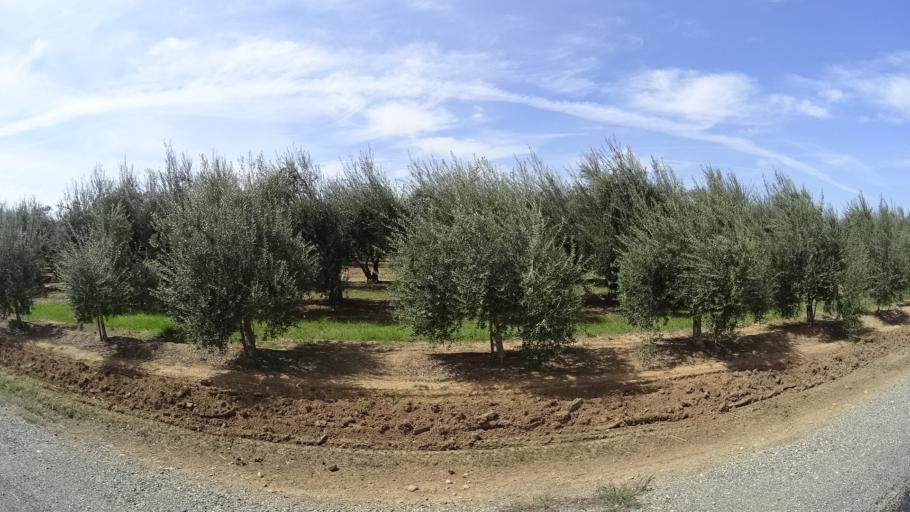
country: US
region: California
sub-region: Glenn County
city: Orland
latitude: 39.7933
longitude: -122.1504
